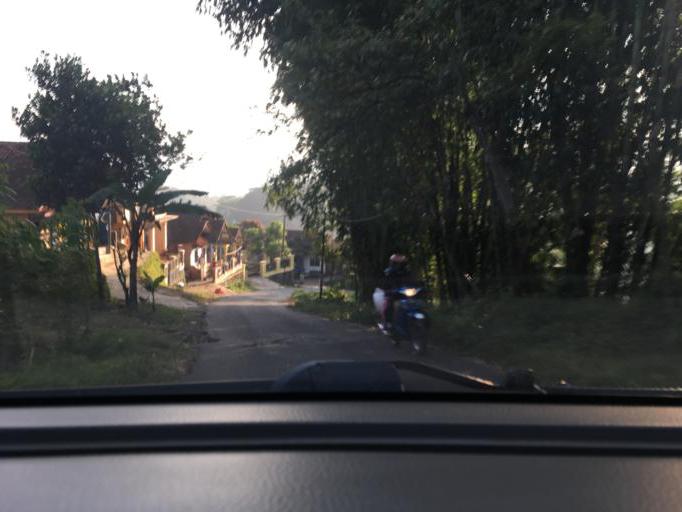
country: ID
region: West Java
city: Maniis
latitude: -7.0428
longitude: 108.3135
